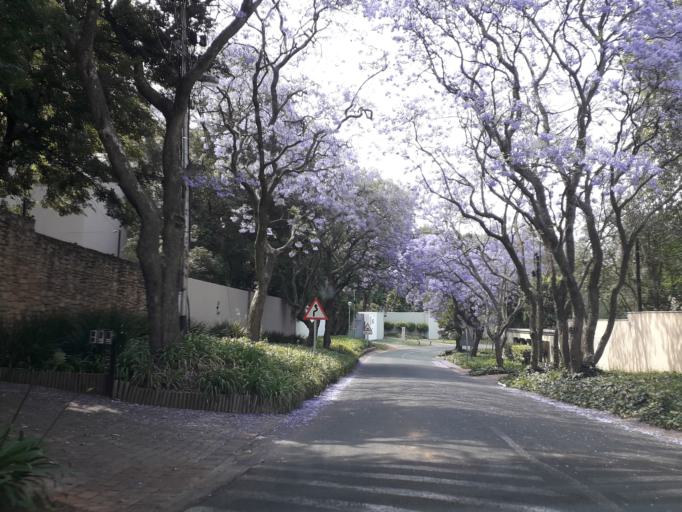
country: ZA
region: Gauteng
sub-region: City of Johannesburg Metropolitan Municipality
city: Johannesburg
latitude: -26.1205
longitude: 28.0580
